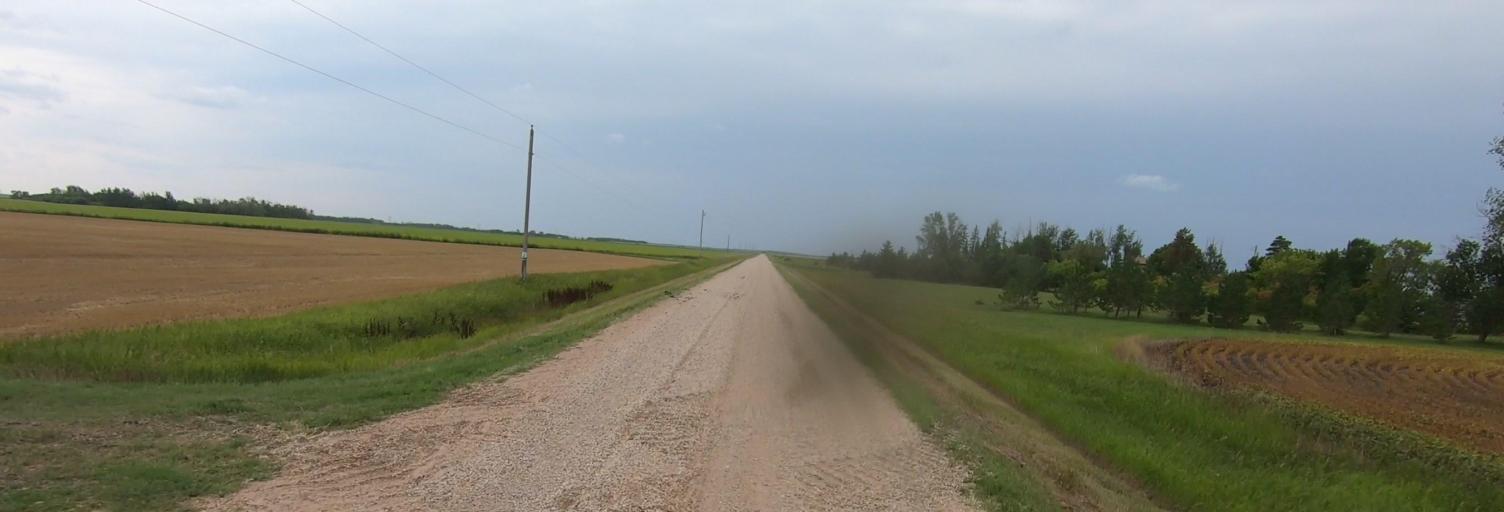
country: CA
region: Manitoba
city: Headingley
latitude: 49.7329
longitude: -97.4136
